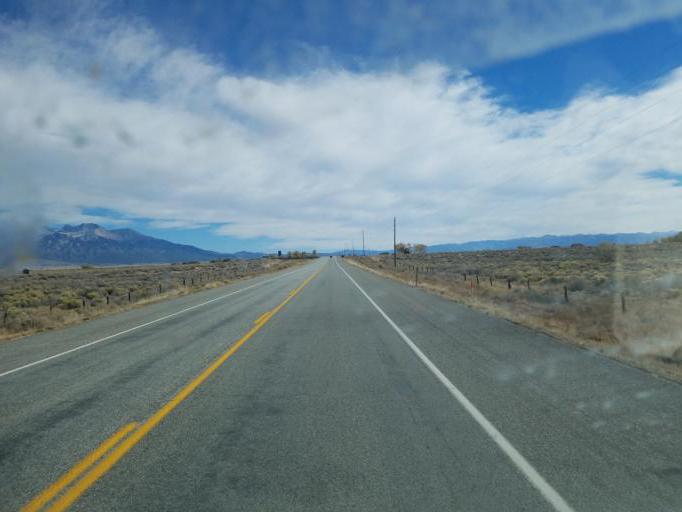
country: US
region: Colorado
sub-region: Alamosa County
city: Alamosa East
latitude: 37.4742
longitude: -105.7445
